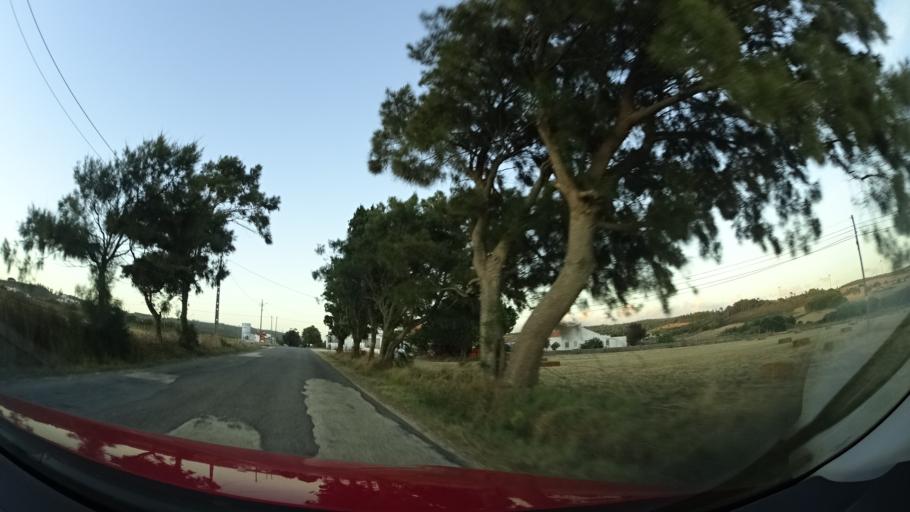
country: PT
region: Faro
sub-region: Aljezur
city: Aljezur
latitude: 37.2371
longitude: -8.8268
